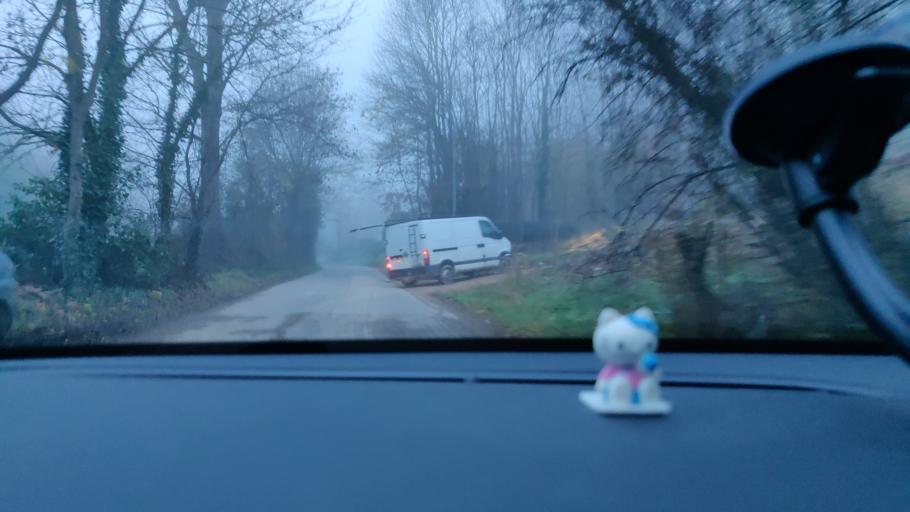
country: FR
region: Midi-Pyrenees
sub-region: Departement de la Haute-Garonne
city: Ramonville-Saint-Agne
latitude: 43.5323
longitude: 1.4641
